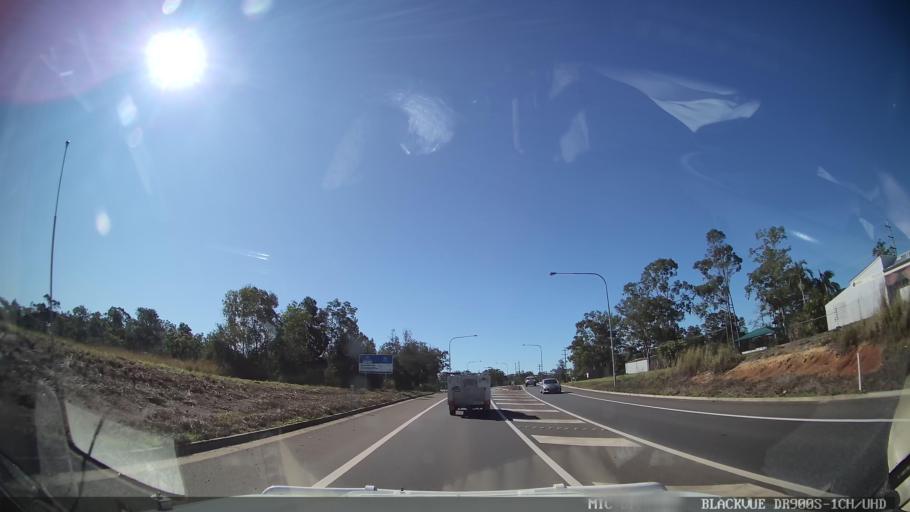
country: AU
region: Queensland
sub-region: Fraser Coast
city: Maryborough
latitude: -25.5160
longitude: 152.6706
